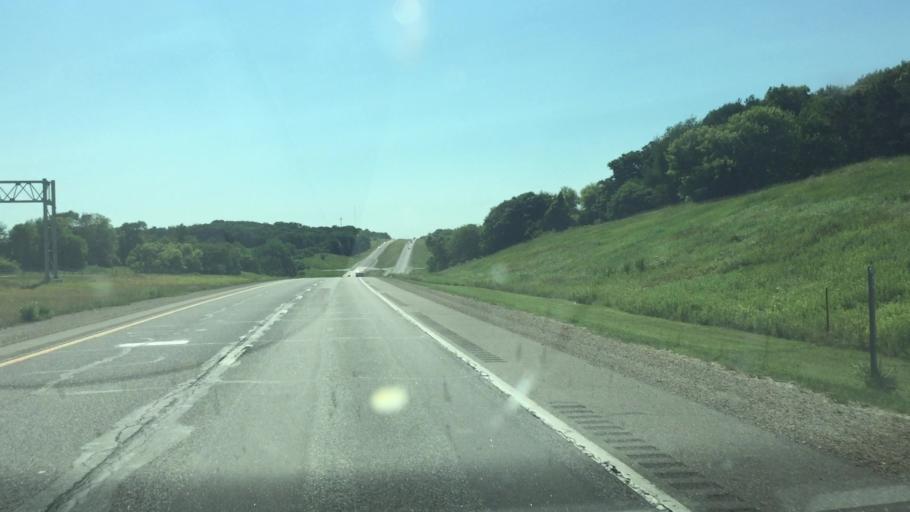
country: US
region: Iowa
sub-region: Linn County
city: Ely
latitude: 41.9254
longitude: -91.5704
